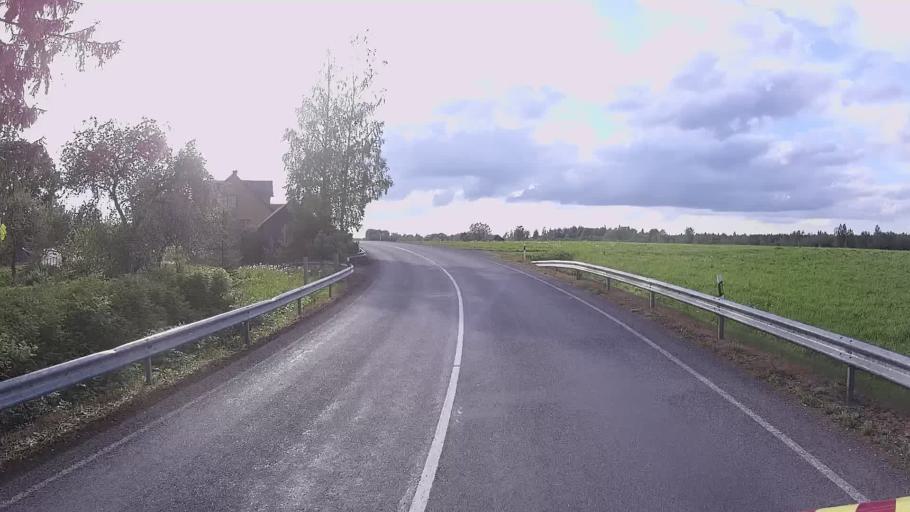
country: EE
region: Jogevamaa
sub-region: Mustvee linn
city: Mustvee
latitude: 59.0474
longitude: 27.0416
